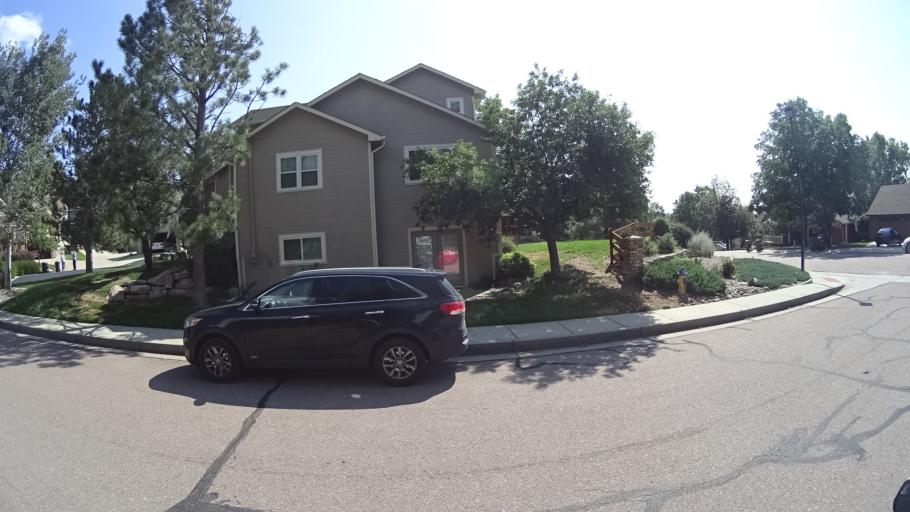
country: US
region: Colorado
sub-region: El Paso County
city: Manitou Springs
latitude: 38.9097
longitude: -104.8726
